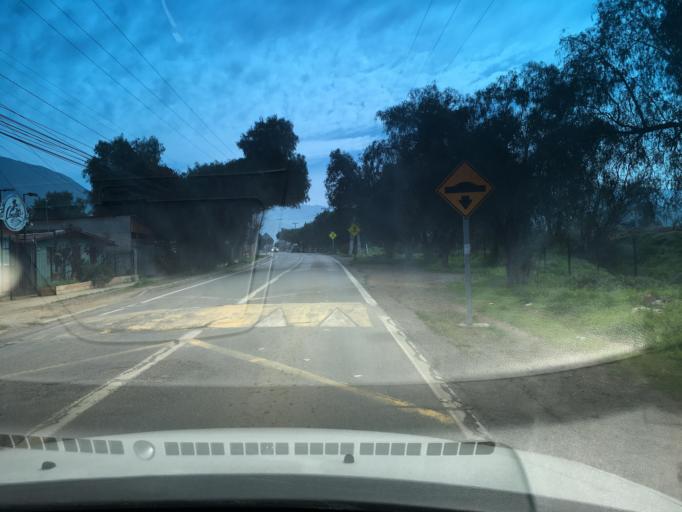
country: CL
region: Santiago Metropolitan
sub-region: Provincia de Chacabuco
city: Lampa
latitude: -33.0907
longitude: -70.9288
